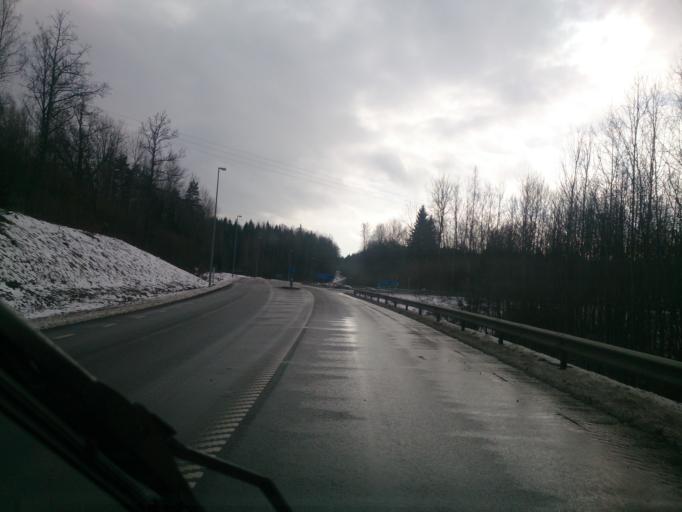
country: SE
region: OEstergoetland
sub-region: Atvidabergs Kommun
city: Atvidaberg
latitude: 58.1851
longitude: 16.0233
